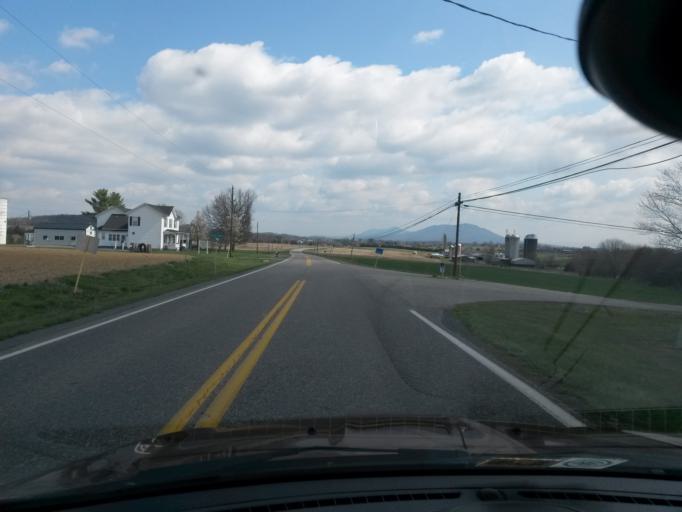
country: US
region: Virginia
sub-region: Augusta County
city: Weyers Cave
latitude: 38.3182
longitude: -78.8794
